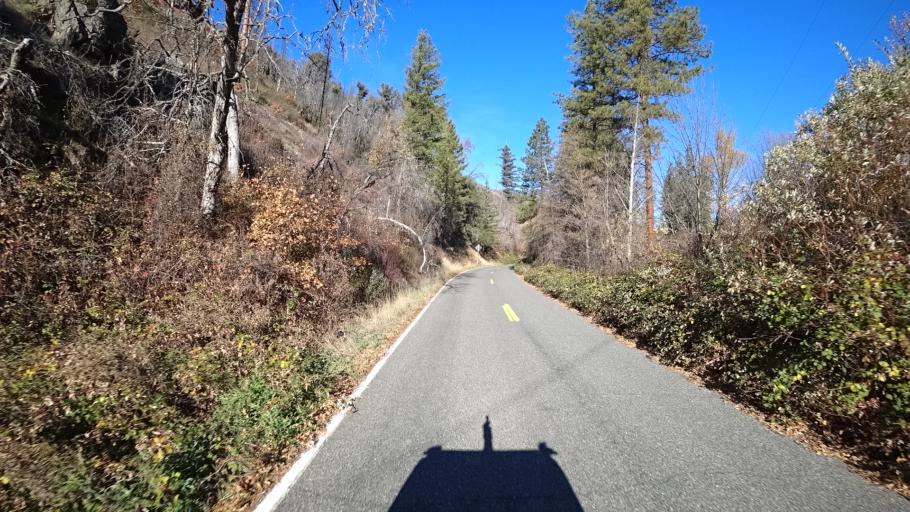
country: US
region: California
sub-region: Siskiyou County
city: Yreka
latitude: 41.8733
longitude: -122.8194
